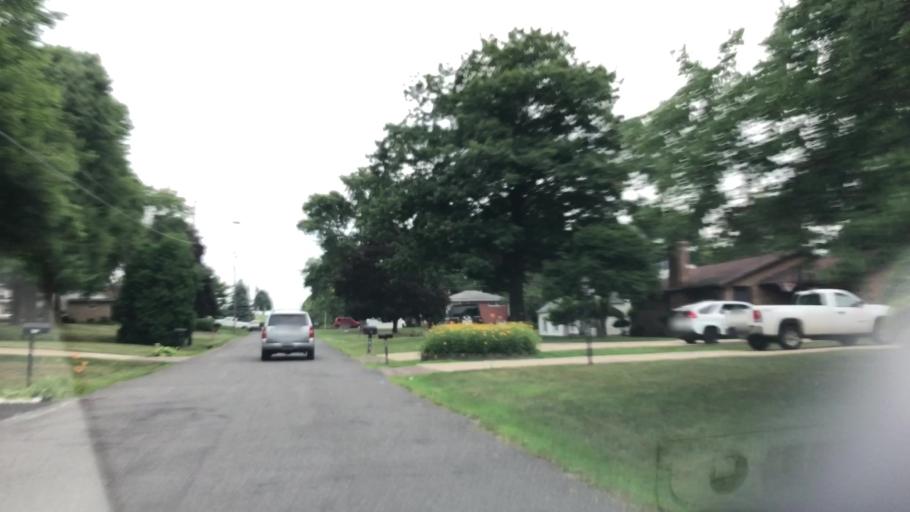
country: US
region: Ohio
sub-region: Stark County
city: North Canton
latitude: 40.8518
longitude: -81.3843
